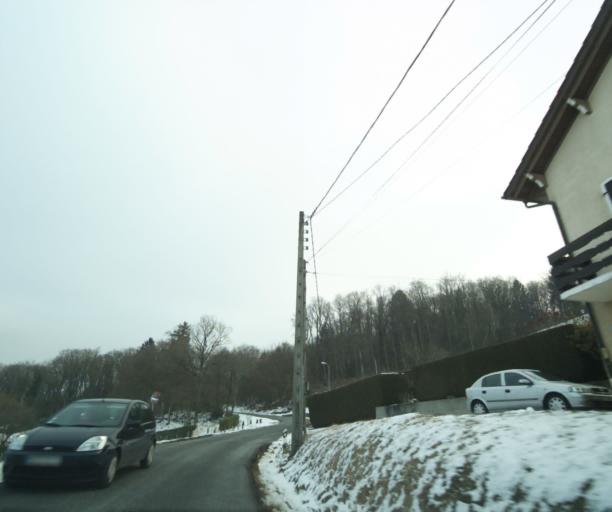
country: FR
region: Rhone-Alpes
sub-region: Departement de la Haute-Savoie
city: Vetraz-Monthoux
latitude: 46.1555
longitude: 6.2381
